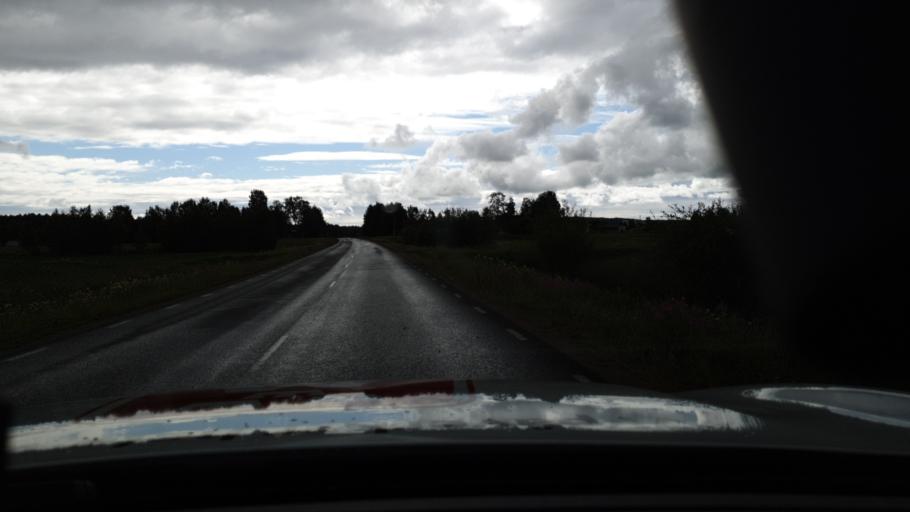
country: SE
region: Norrbotten
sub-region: Pitea Kommun
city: Rosvik
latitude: 65.5279
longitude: 21.8056
